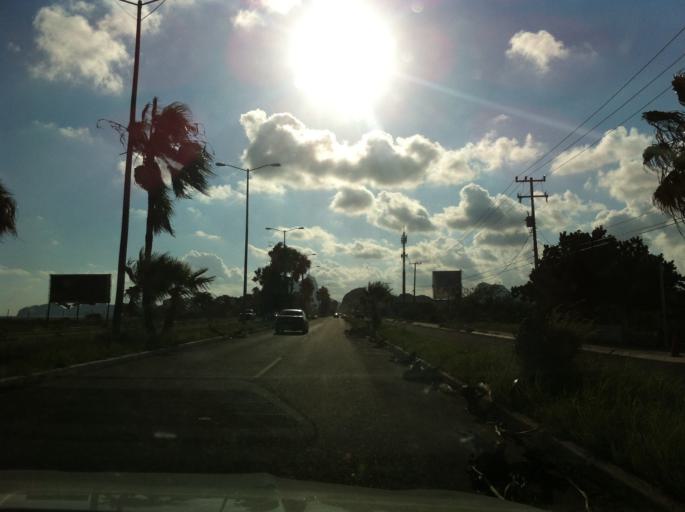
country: MX
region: Sonora
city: Heroica Guaymas
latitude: 27.9658
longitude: -111.0156
